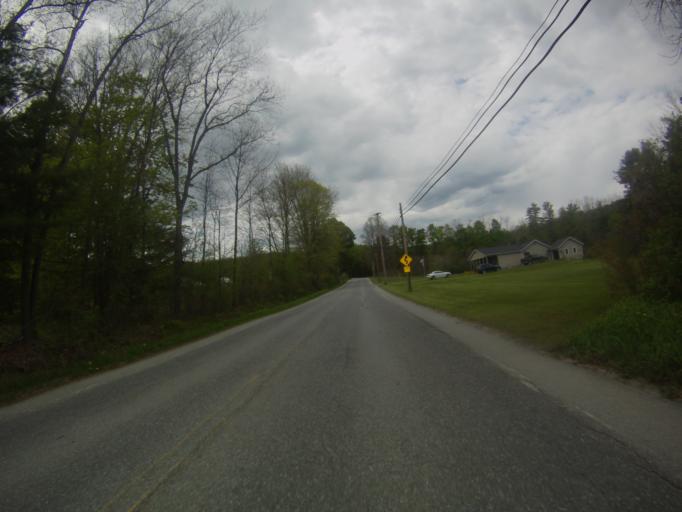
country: US
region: New York
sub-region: Essex County
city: Port Henry
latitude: 43.9529
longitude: -73.4829
